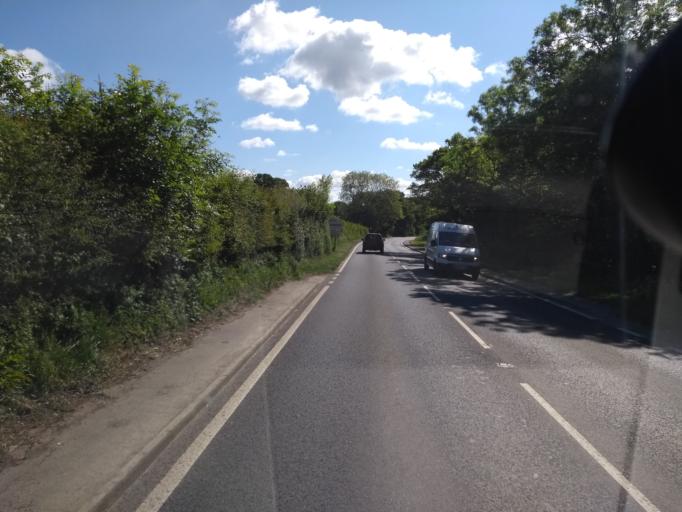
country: GB
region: England
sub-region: Somerset
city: Bridgwater
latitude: 51.1297
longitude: -3.0354
